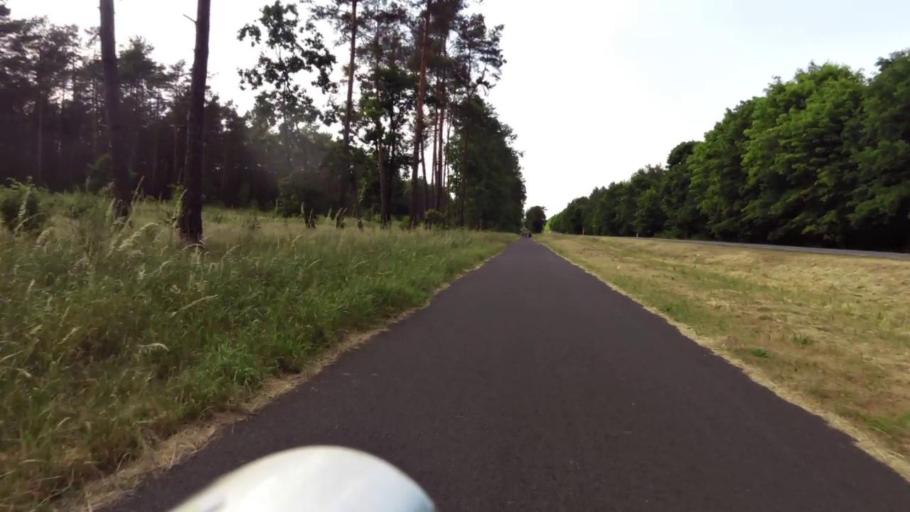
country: PL
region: Kujawsko-Pomorskie
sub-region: Powiat torunski
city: Lysomice
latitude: 53.0724
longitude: 18.5451
